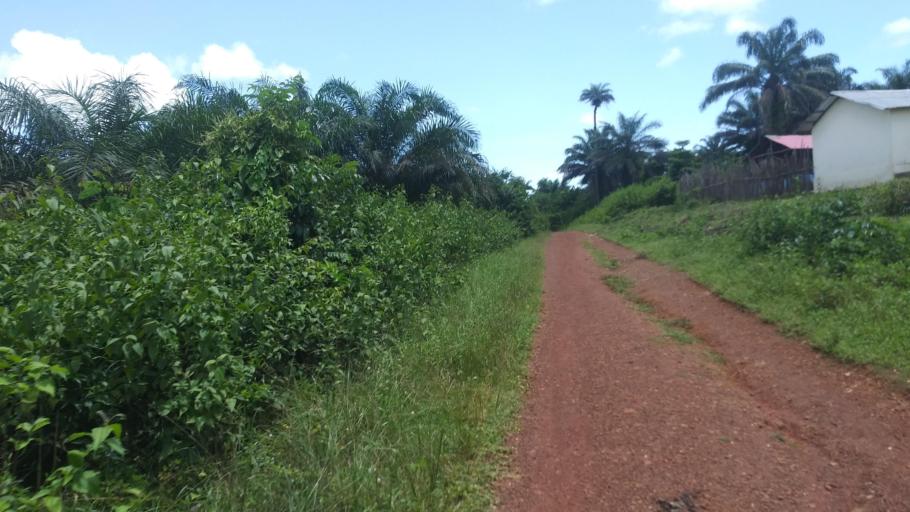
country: SL
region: Northern Province
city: Binkolo
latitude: 8.9022
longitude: -11.9878
